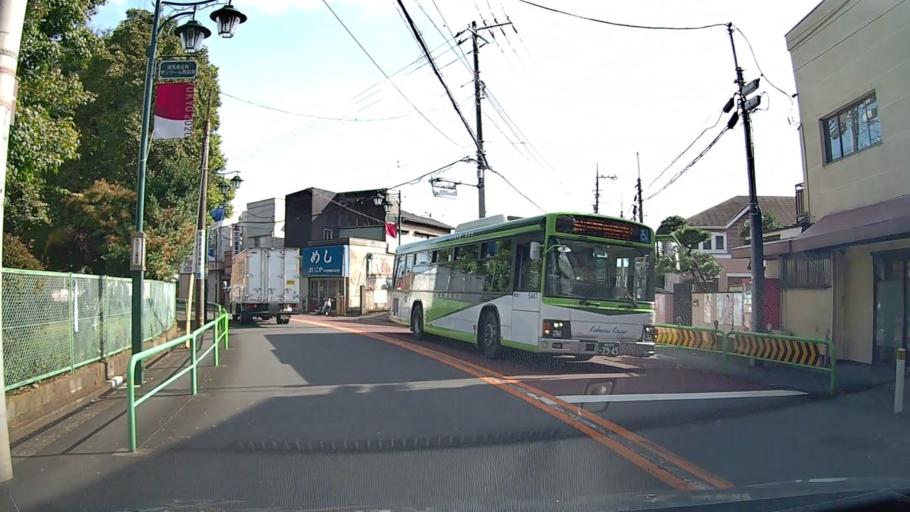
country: JP
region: Saitama
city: Wako
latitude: 35.7495
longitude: 139.6403
